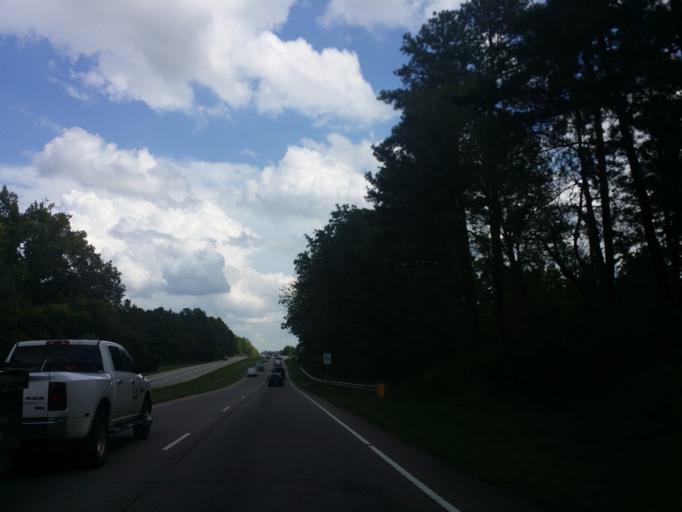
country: US
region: North Carolina
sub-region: Wake County
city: Morrisville
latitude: 35.9234
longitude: -78.7975
